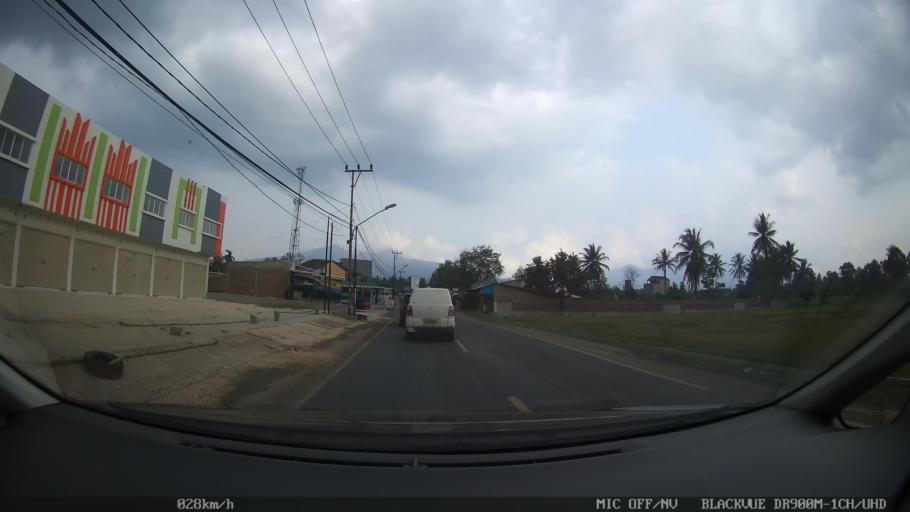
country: ID
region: Lampung
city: Gedongtataan
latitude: -5.3781
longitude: 105.0933
